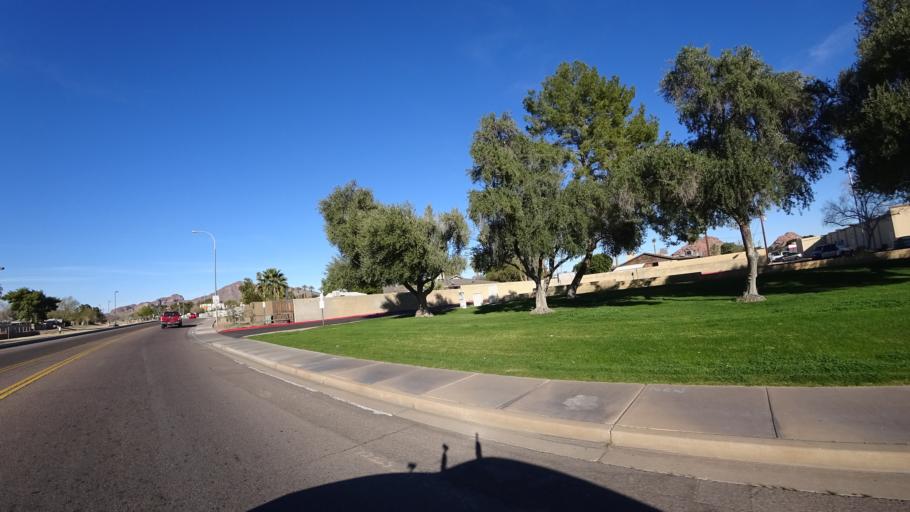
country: US
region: Arizona
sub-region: Maricopa County
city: Tempe Junction
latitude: 33.4670
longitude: -111.9784
